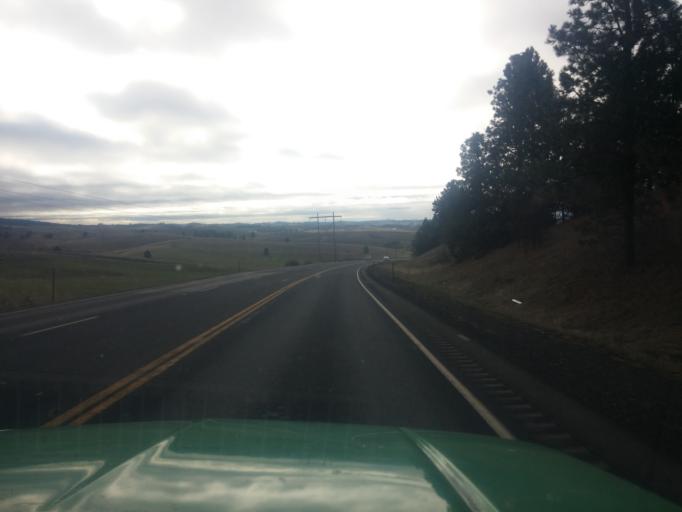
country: US
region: Idaho
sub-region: Latah County
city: Moscow
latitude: 46.8047
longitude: -117.0009
